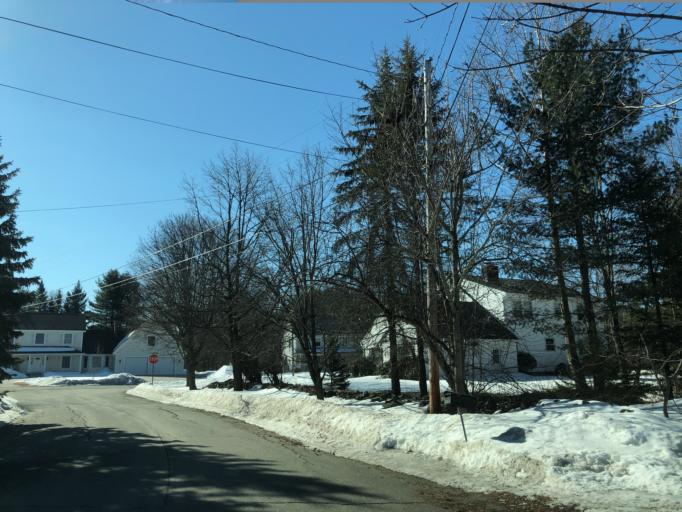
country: US
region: Maine
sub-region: Penobscot County
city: Brewer
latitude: 44.8206
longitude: -68.7489
